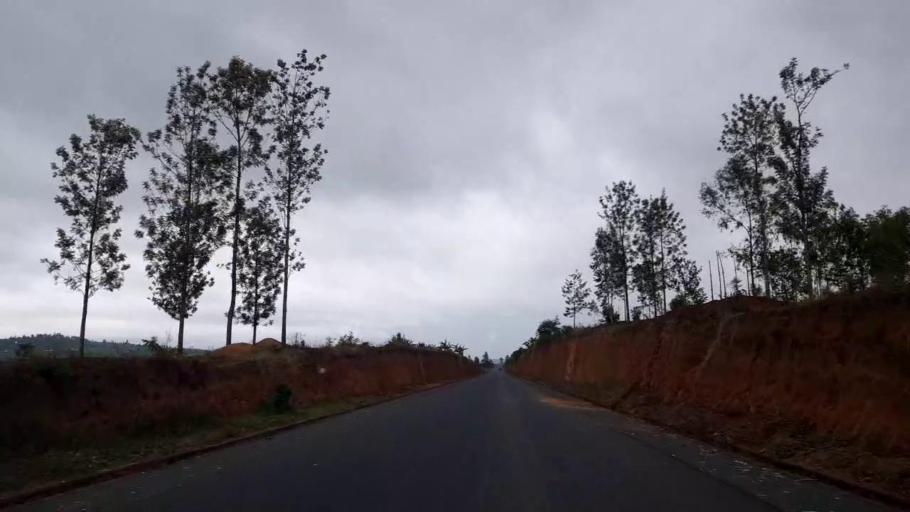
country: RW
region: Northern Province
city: Byumba
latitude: -1.4320
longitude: 30.2621
